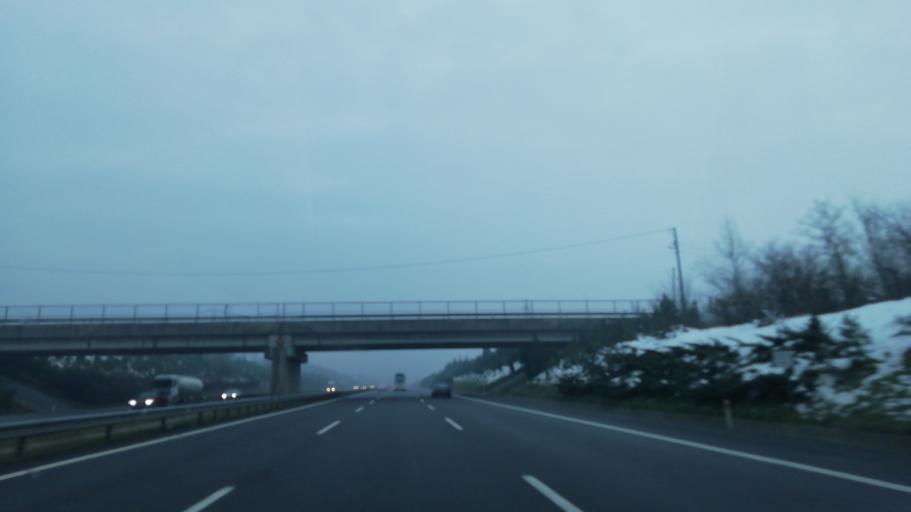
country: TR
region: Duzce
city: Kaynasli
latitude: 40.7806
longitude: 31.3418
